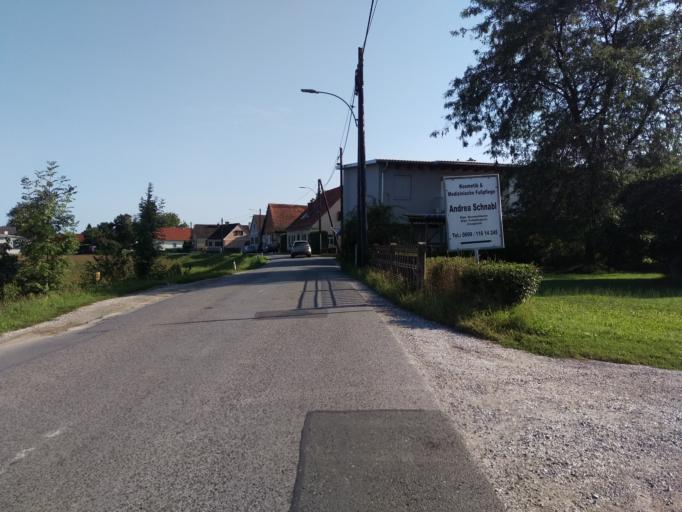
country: AT
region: Styria
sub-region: Politischer Bezirk Graz-Umgebung
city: Feldkirchen bei Graz
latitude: 47.0201
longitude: 15.4437
